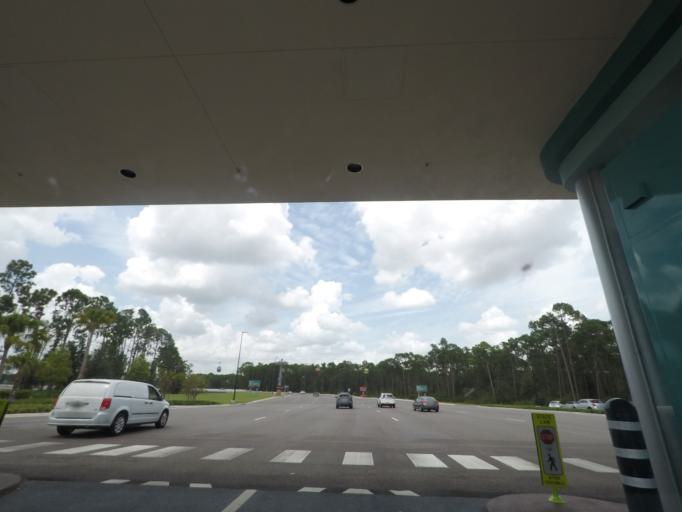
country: US
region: Florida
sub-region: Osceola County
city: Celebration
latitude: 28.3574
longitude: -81.5514
